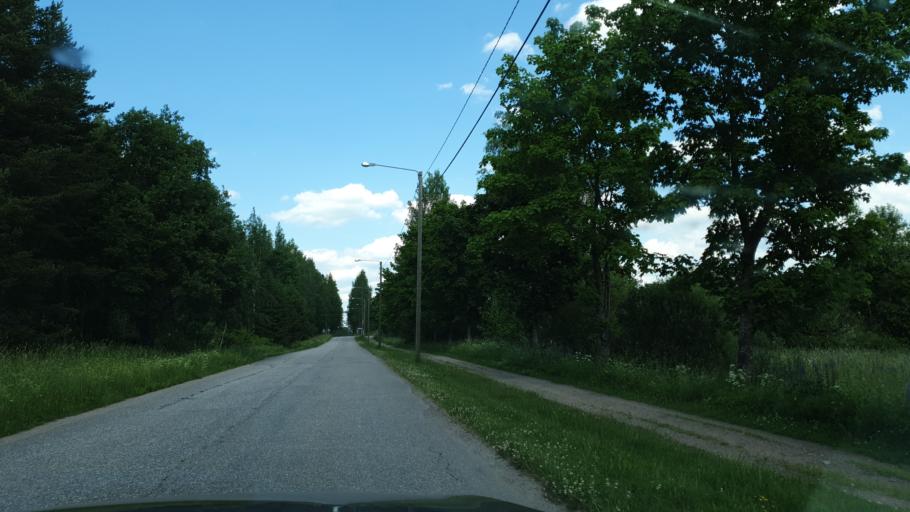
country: FI
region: Uusimaa
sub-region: Helsinki
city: Vihti
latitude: 60.3779
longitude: 24.5101
